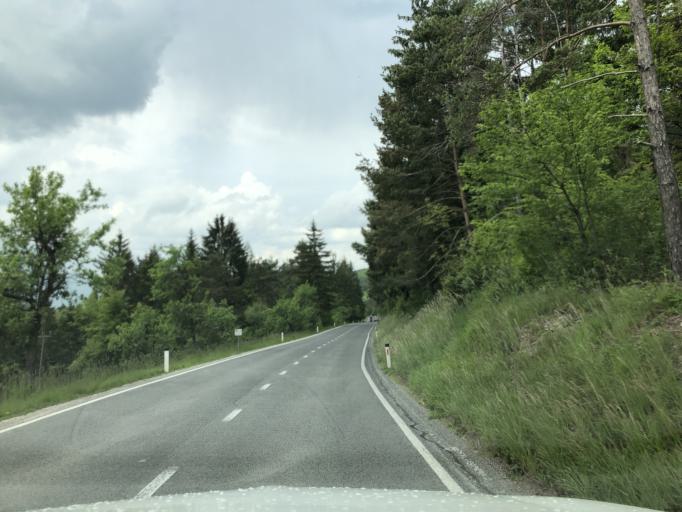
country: SI
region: Bloke
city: Nova Vas
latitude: 45.7601
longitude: 14.4637
